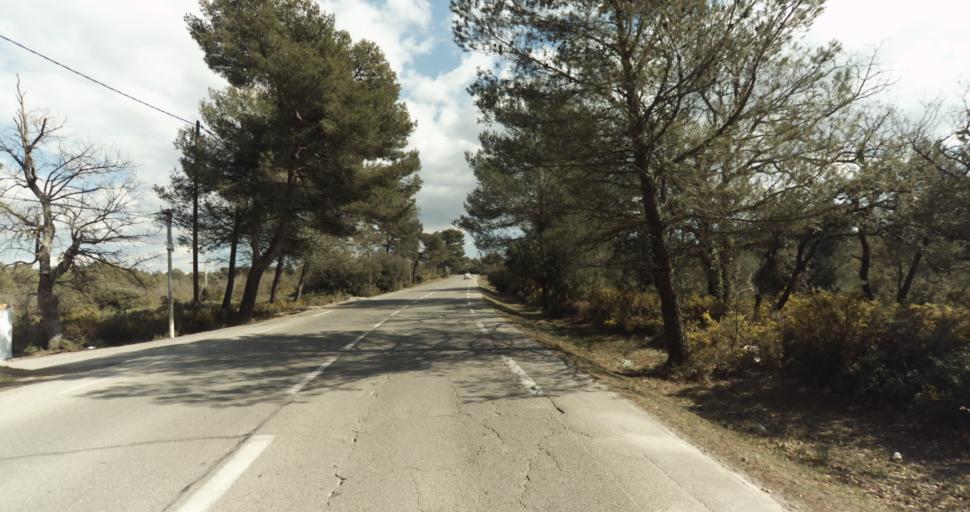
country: FR
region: Provence-Alpes-Cote d'Azur
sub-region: Departement des Bouches-du-Rhone
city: Mimet
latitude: 43.4487
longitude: 5.5108
